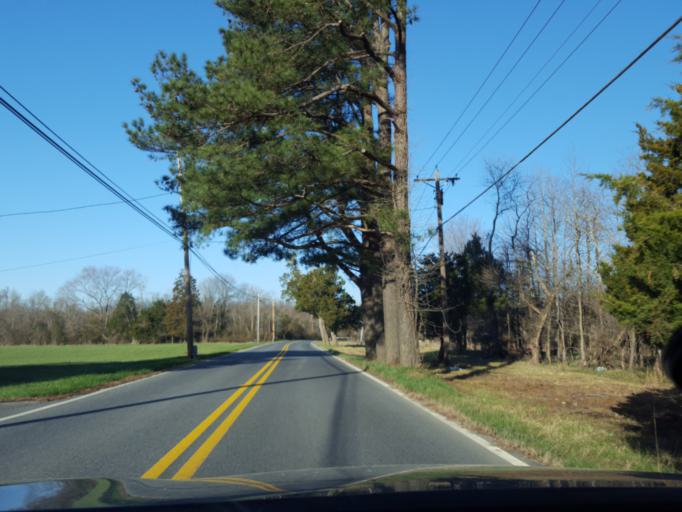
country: US
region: Maryland
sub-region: Prince George's County
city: Baden
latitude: 38.6629
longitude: -76.8177
